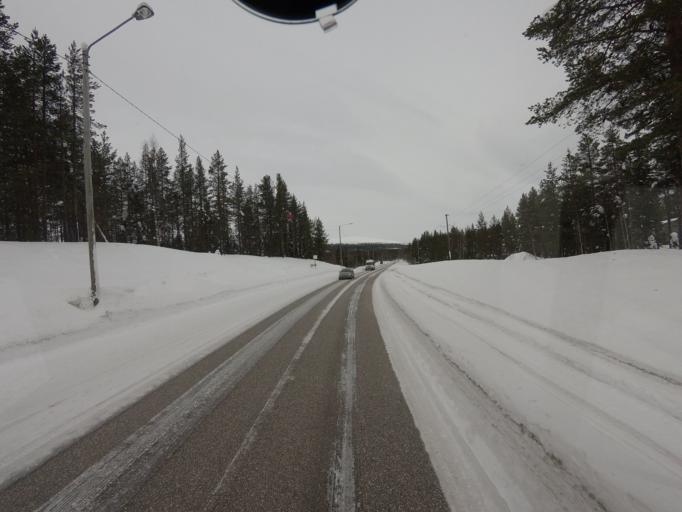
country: FI
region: Lapland
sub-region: Tunturi-Lappi
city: Kolari
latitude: 67.5342
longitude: 24.2782
